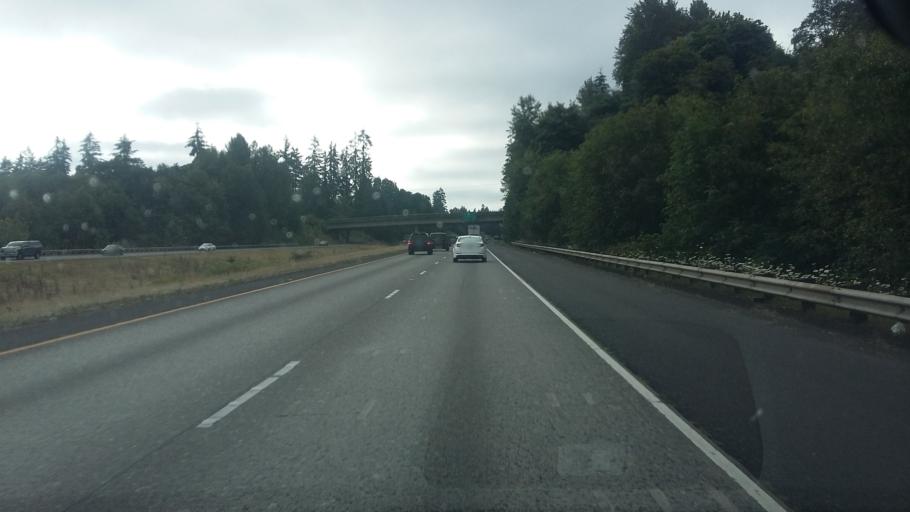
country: US
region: Washington
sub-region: Clark County
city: Salmon Creek
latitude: 45.7091
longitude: -122.6353
